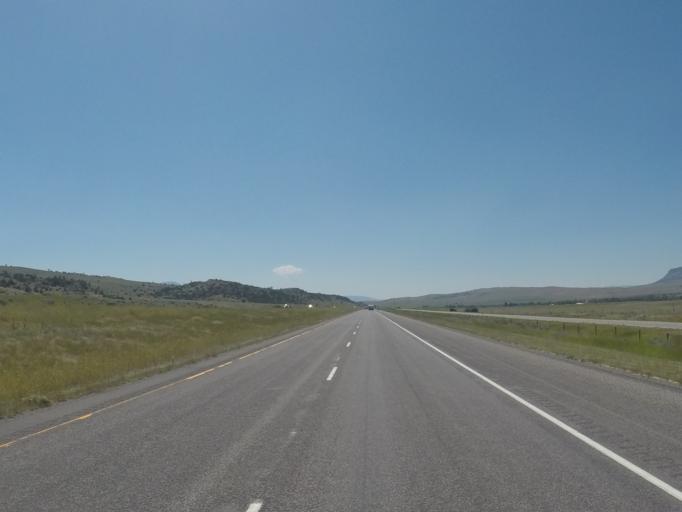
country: US
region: Montana
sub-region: Sweet Grass County
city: Big Timber
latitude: 45.7428
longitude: -110.1930
